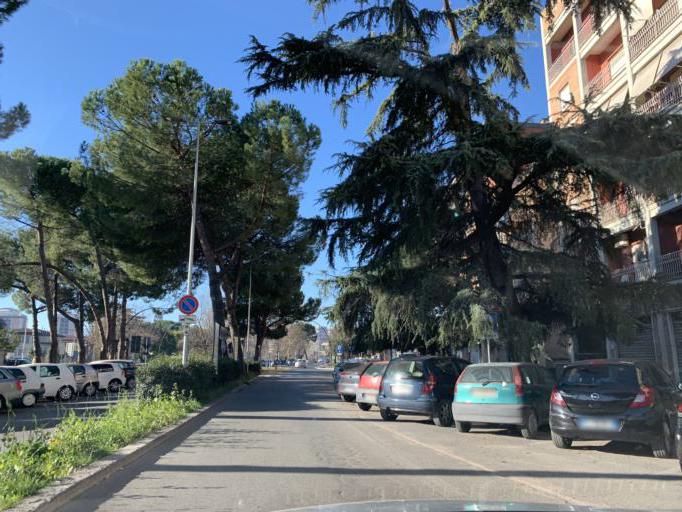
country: IT
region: Umbria
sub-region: Provincia di Terni
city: Terni
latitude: 42.5605
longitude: 12.6504
